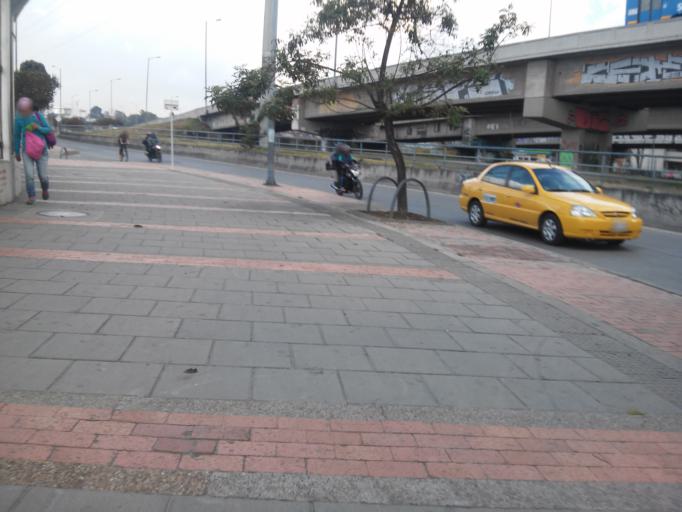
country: CO
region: Cundinamarca
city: Soacha
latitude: 4.5964
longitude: -74.1614
